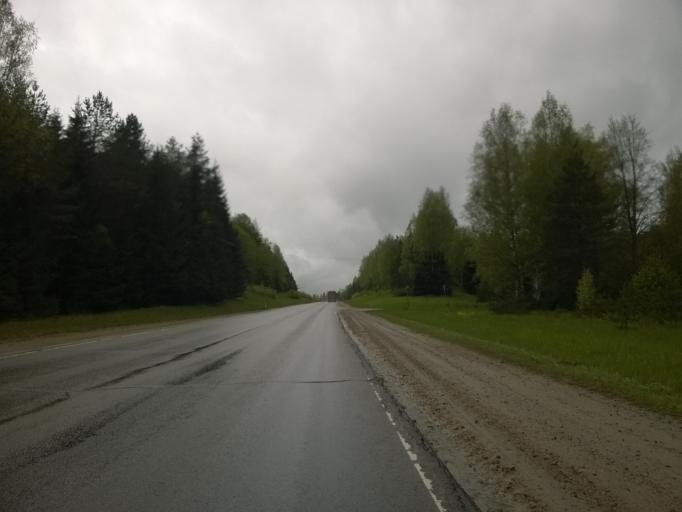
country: LV
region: Amatas Novads
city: Drabesi
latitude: 57.2209
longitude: 25.2265
